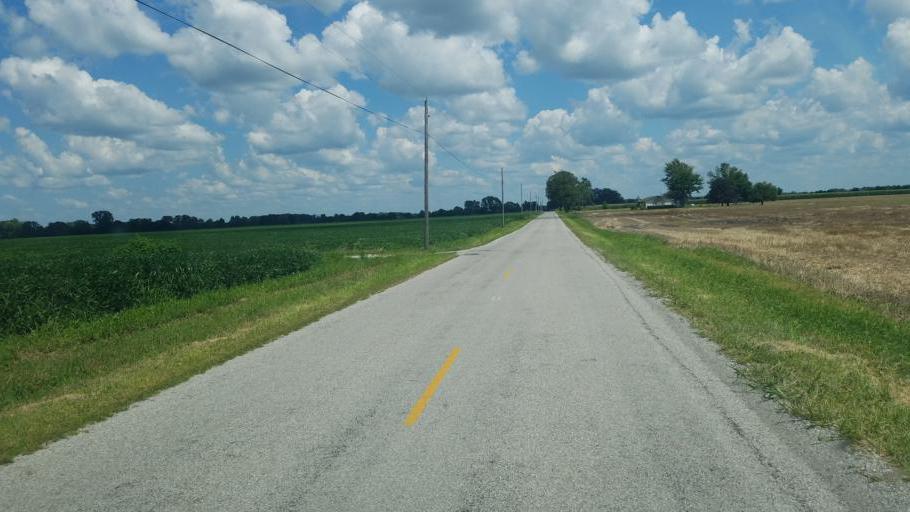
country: US
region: Ohio
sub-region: Marion County
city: Marion
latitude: 40.6377
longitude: -83.0101
